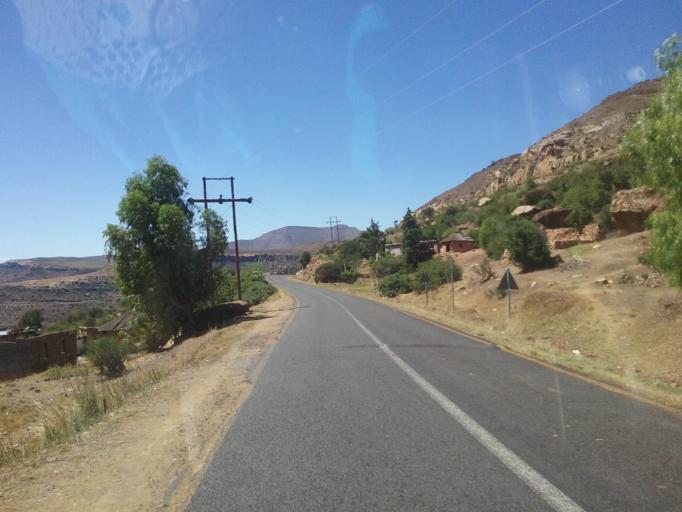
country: LS
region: Quthing
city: Quthing
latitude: -30.2788
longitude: 27.7469
